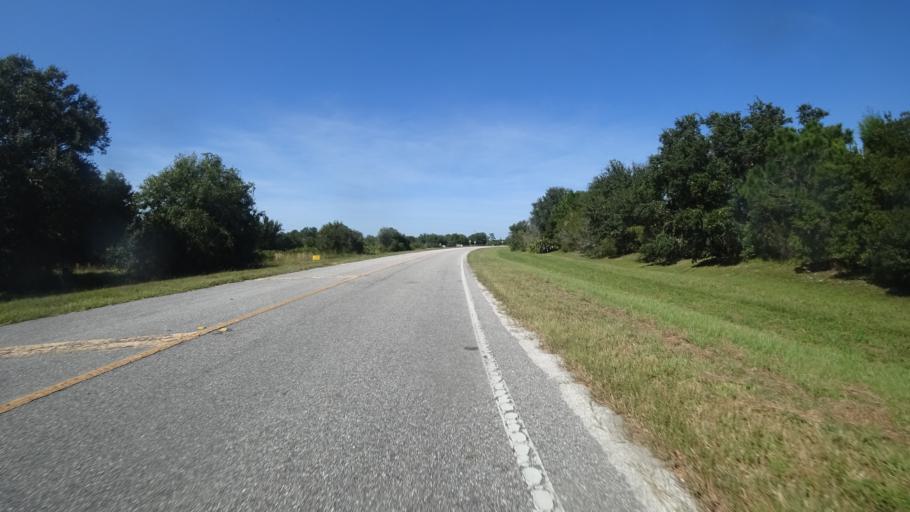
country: US
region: Florida
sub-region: Sarasota County
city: Fruitville
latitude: 27.3989
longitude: -82.3029
